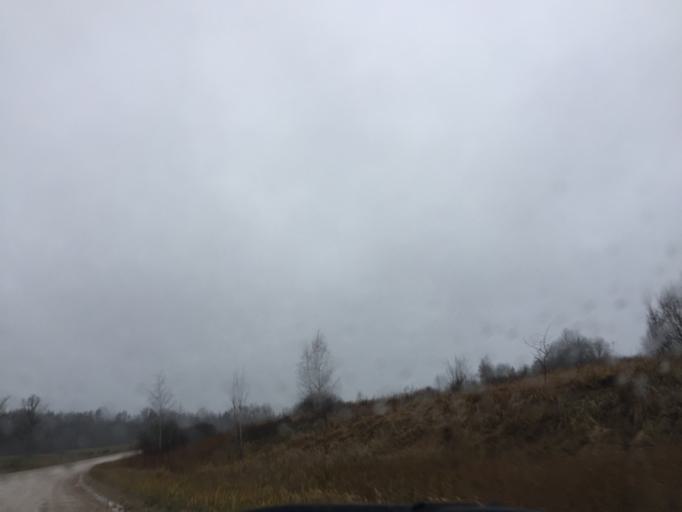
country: LV
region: Salas
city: Sala
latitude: 56.4925
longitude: 25.6803
